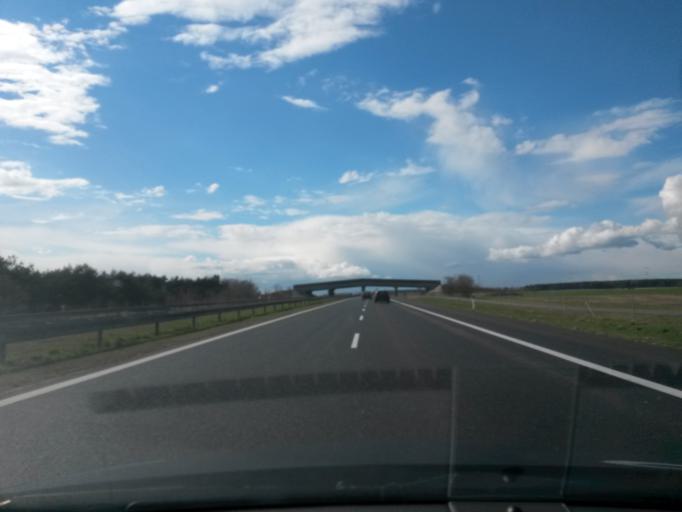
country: PL
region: Greater Poland Voivodeship
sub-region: Powiat slupecki
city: Strzalkowo
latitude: 52.2671
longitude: 17.7353
